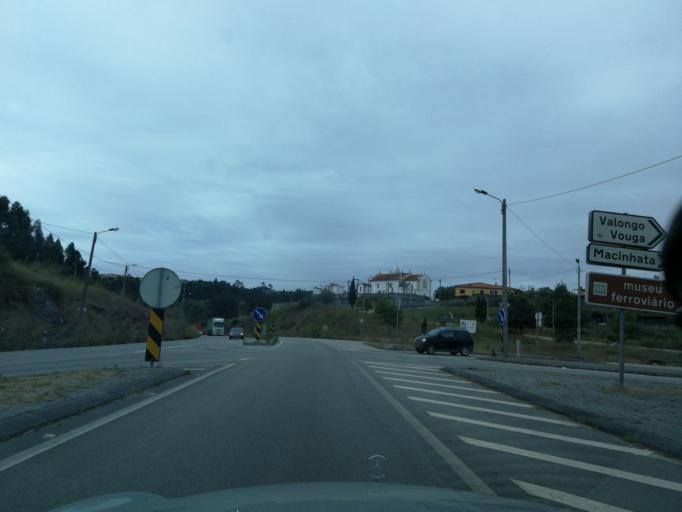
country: PT
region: Aveiro
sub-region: Agueda
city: Valongo
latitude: 40.6369
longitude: -8.4703
